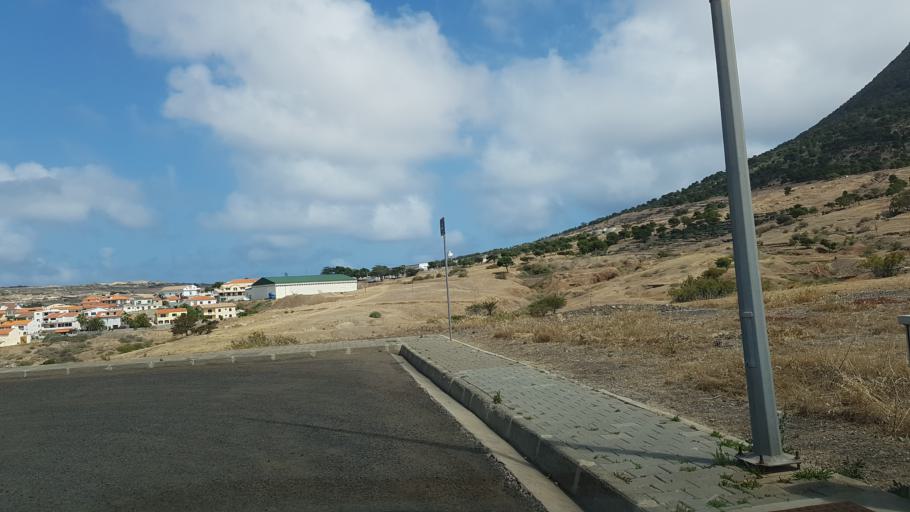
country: PT
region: Madeira
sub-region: Porto Santo
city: Vila de Porto Santo
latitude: 33.0683
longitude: -16.3352
